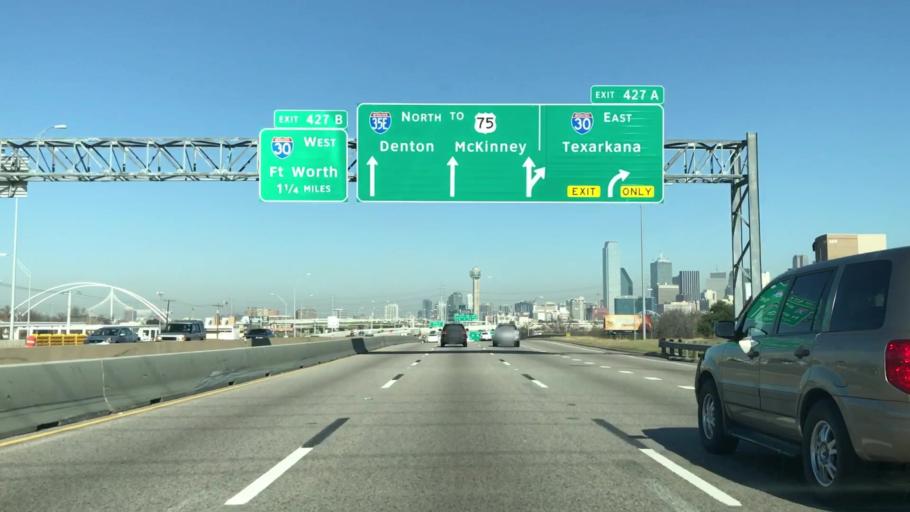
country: US
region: Texas
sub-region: Dallas County
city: Dallas
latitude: 32.7530
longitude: -96.8093
